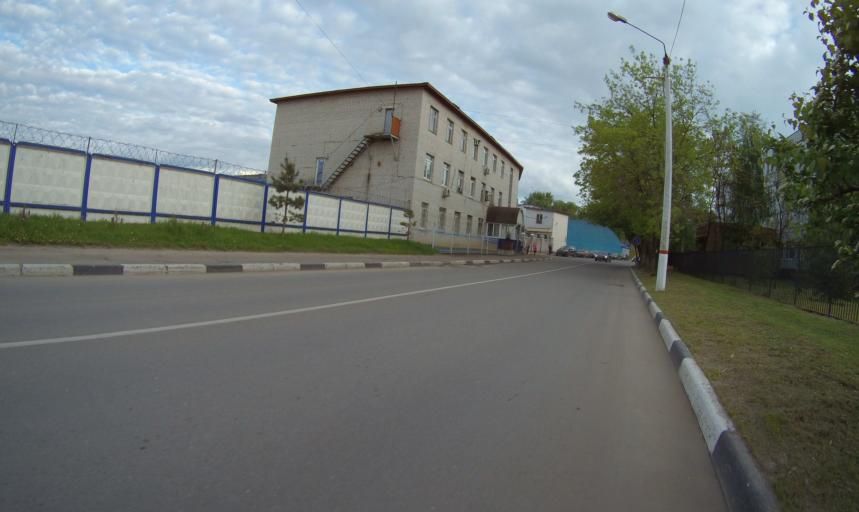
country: RU
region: Moskovskaya
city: Ramenskoye
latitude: 55.5717
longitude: 38.2465
